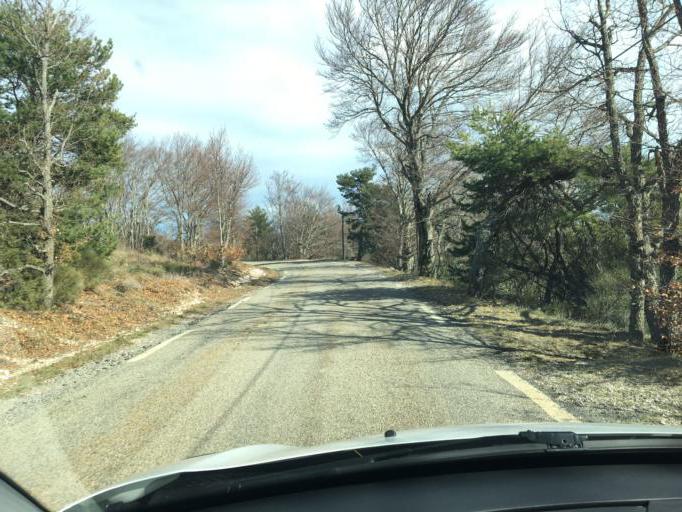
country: FR
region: Provence-Alpes-Cote d'Azur
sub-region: Departement du Vaucluse
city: Saint-Saturnin-les-Apt
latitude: 43.9741
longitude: 5.4642
